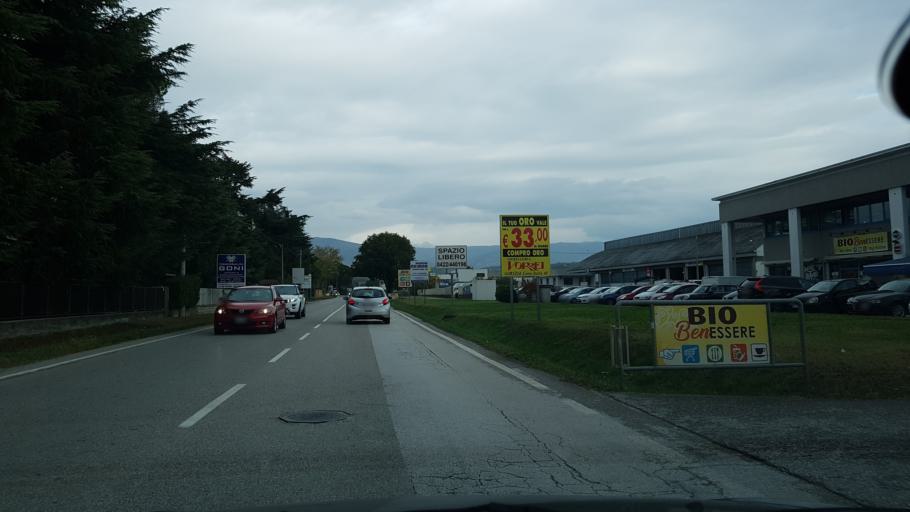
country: IT
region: Friuli Venezia Giulia
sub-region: Provincia di Gorizia
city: Gorizia
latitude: 45.9277
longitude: 13.6209
